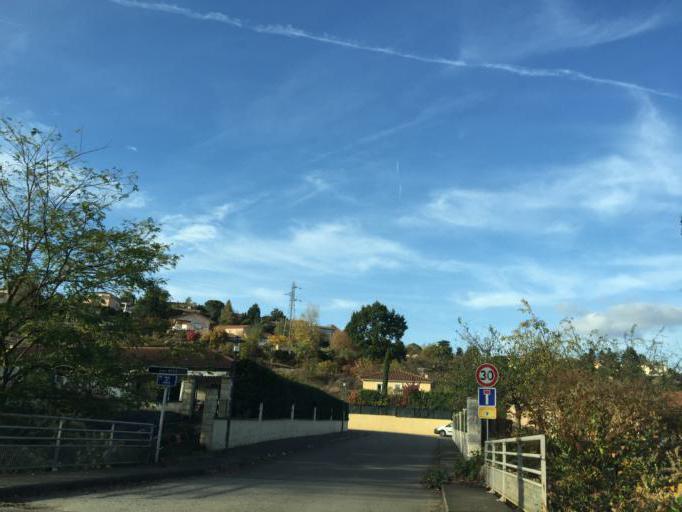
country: FR
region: Rhone-Alpes
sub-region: Departement de la Loire
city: La Grand-Croix
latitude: 45.4957
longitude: 4.5528
